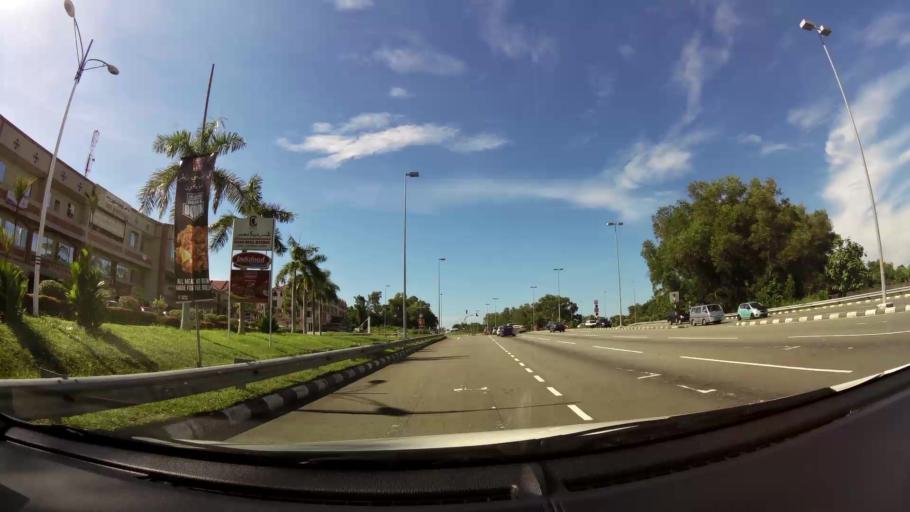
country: BN
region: Brunei and Muara
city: Bandar Seri Begawan
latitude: 4.9620
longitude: 114.9517
